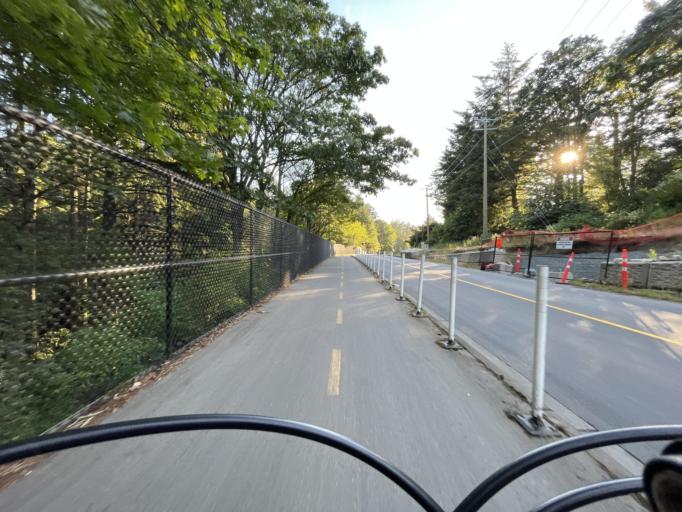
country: CA
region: British Columbia
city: Colwood
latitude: 48.4478
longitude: -123.4748
